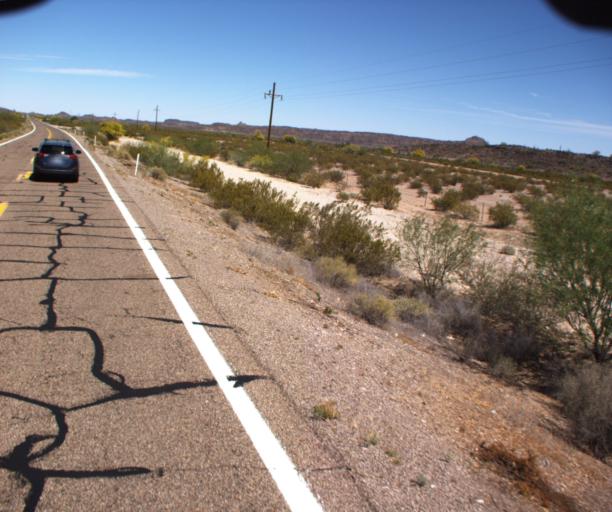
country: US
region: Arizona
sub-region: Pima County
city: Ajo
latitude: 32.5004
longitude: -112.8812
